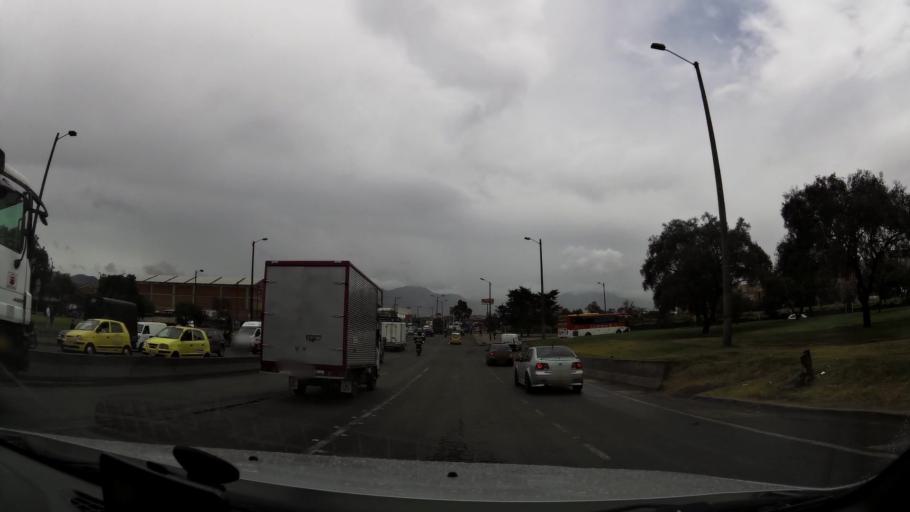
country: CO
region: Bogota D.C.
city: Bogota
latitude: 4.6483
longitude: -74.1260
